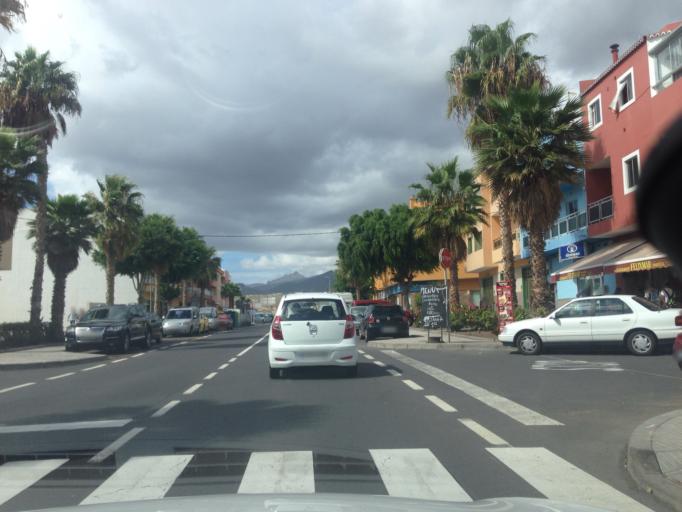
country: ES
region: Canary Islands
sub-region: Provincia de Santa Cruz de Tenerife
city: San Isidro
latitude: 28.0303
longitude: -16.5943
